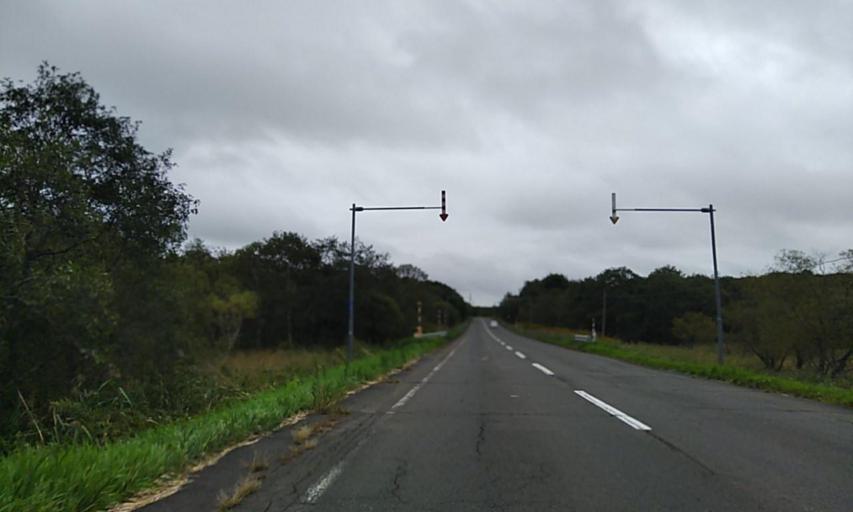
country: JP
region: Hokkaido
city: Nemuro
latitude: 43.2675
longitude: 145.2393
